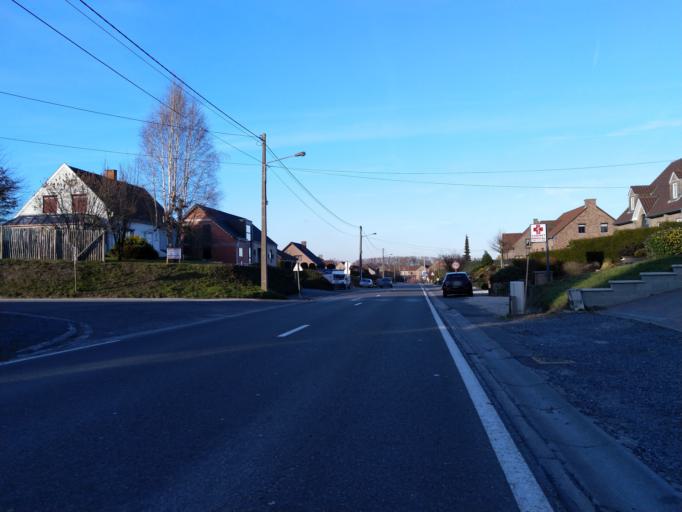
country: BE
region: Wallonia
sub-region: Province du Hainaut
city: Frameries
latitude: 50.3997
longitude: 3.9164
